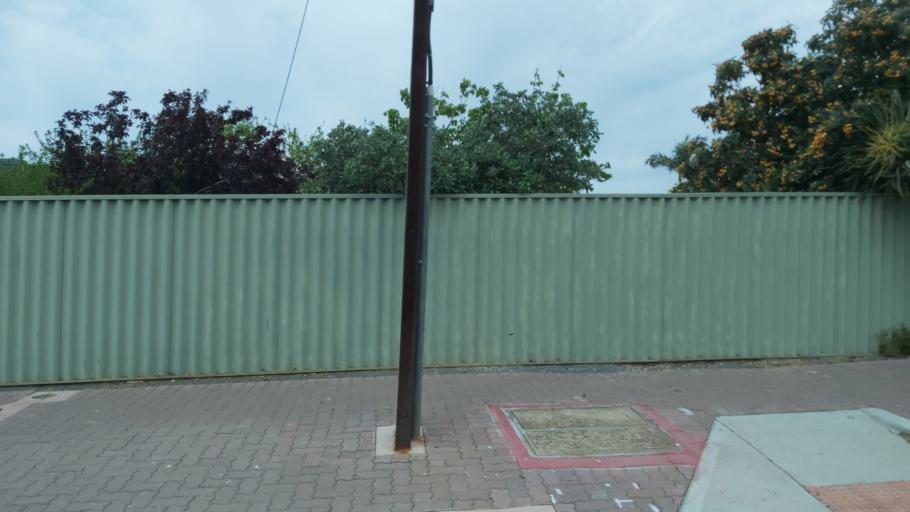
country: AU
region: South Australia
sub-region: Marion
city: Clovelly Park
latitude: -34.9925
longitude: 138.5839
